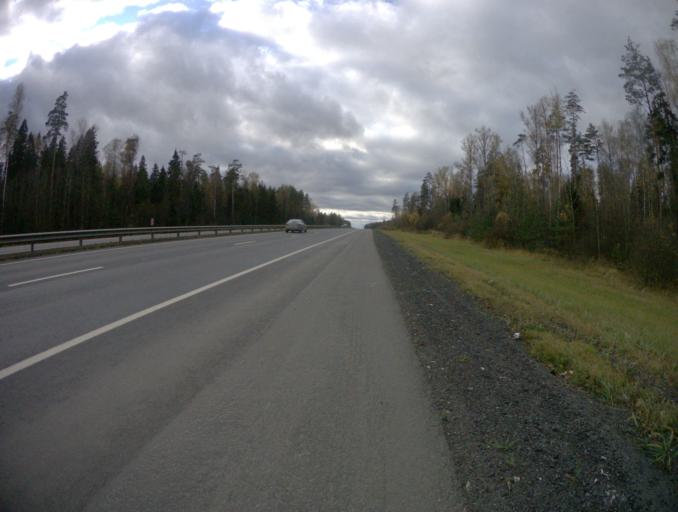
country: RU
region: Vladimir
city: Kommunar
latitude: 56.0919
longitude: 40.5251
